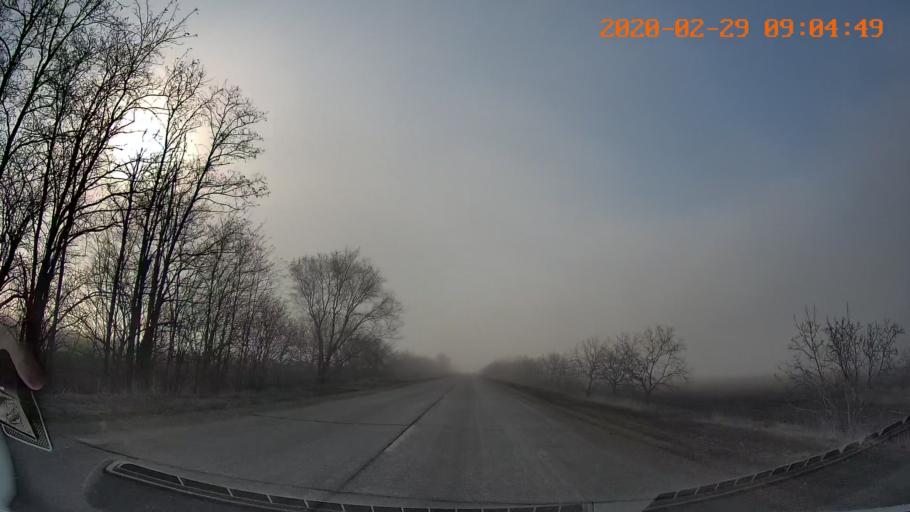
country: MD
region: Telenesti
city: Tiraspolul Nou
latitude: 46.8972
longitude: 29.7377
